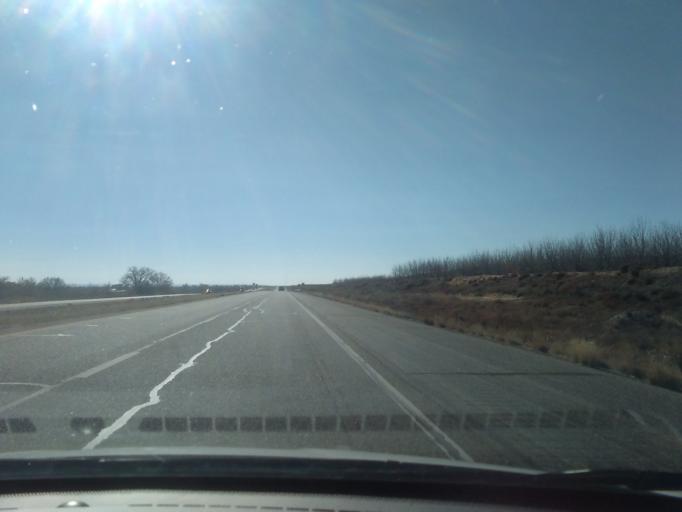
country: US
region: New Mexico
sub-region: Valencia County
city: Jarales
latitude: 34.5766
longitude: -106.7922
